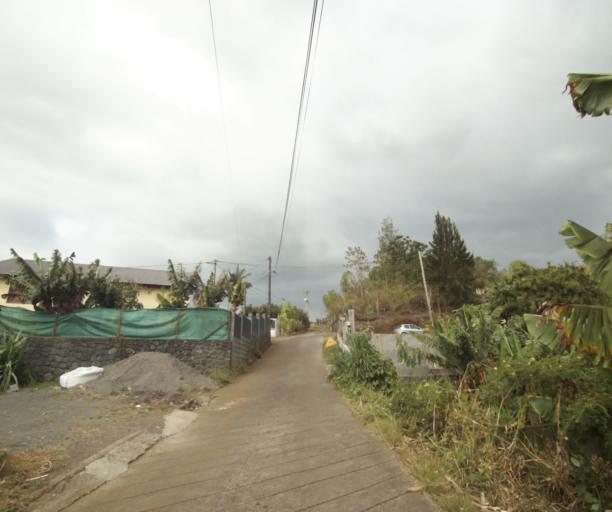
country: RE
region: Reunion
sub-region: Reunion
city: Saint-Paul
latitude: -21.0308
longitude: 55.3125
